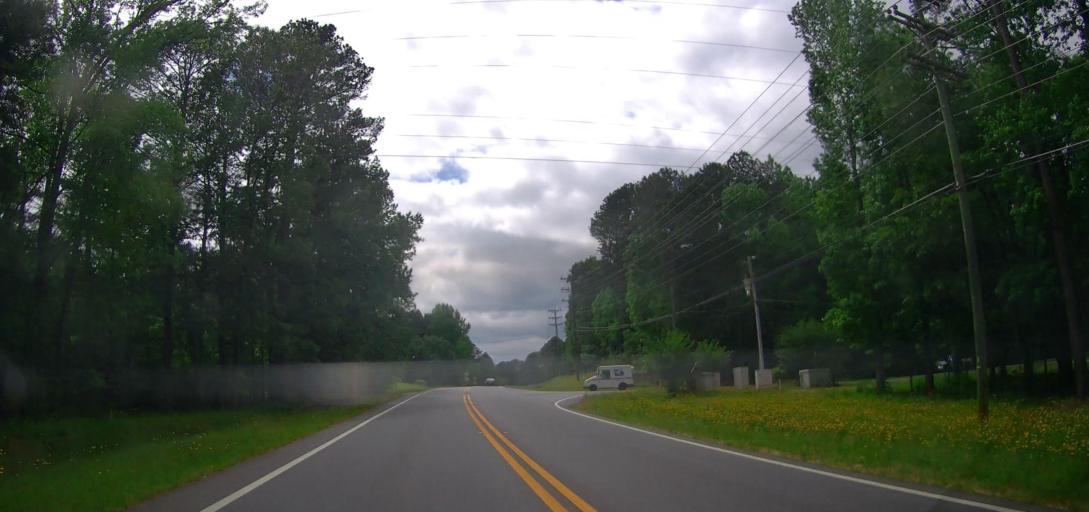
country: US
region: Georgia
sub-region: DeKalb County
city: Pine Mountain
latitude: 33.5927
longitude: -84.1307
